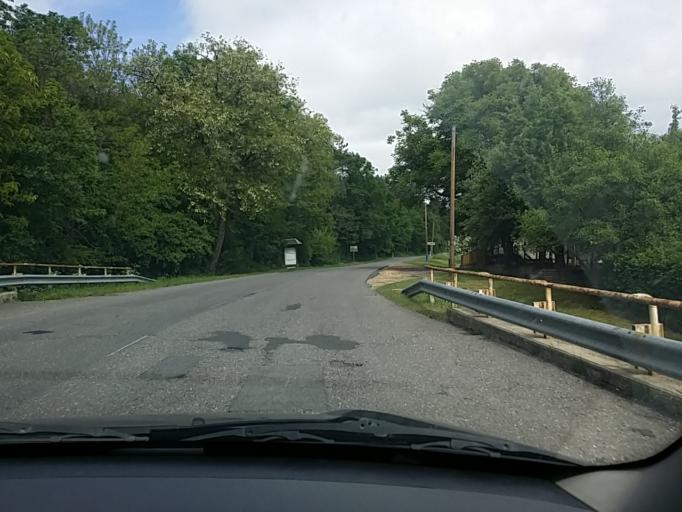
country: HU
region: Borsod-Abauj-Zemplen
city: Sarospatak
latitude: 48.4986
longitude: 21.4864
